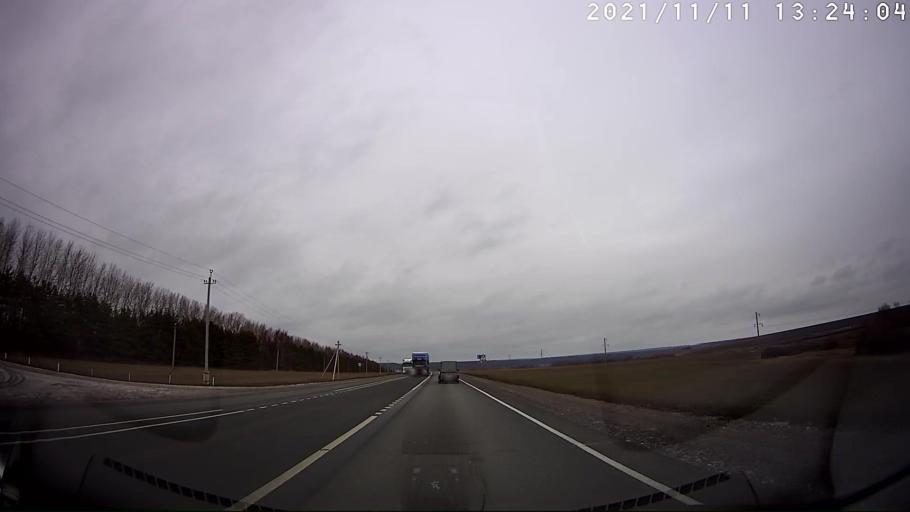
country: RU
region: Chuvashia
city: Komsomol'skoye
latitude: 55.2416
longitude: 47.5584
